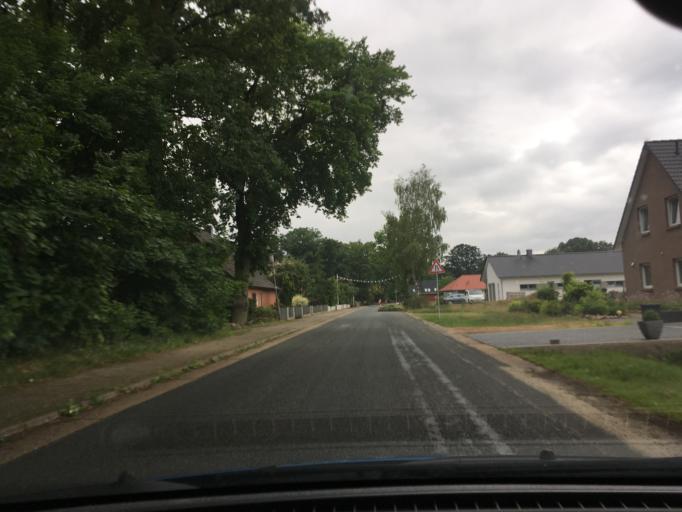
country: DE
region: Lower Saxony
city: Soderstorf
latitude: 53.1432
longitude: 10.1564
